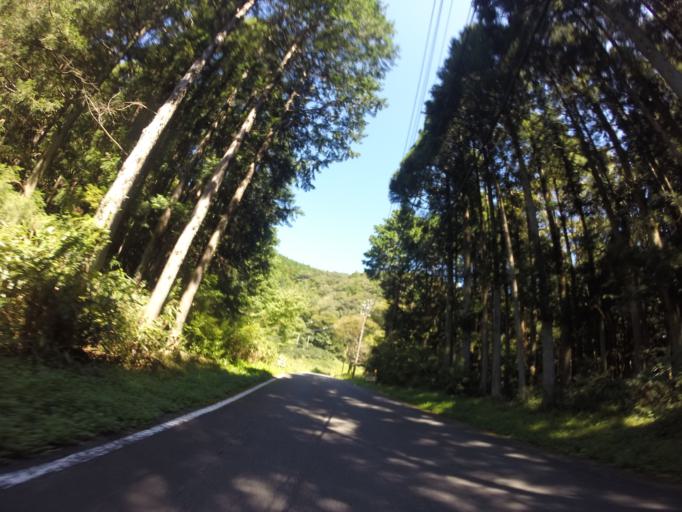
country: JP
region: Shizuoka
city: Fujieda
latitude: 34.9692
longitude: 138.1918
